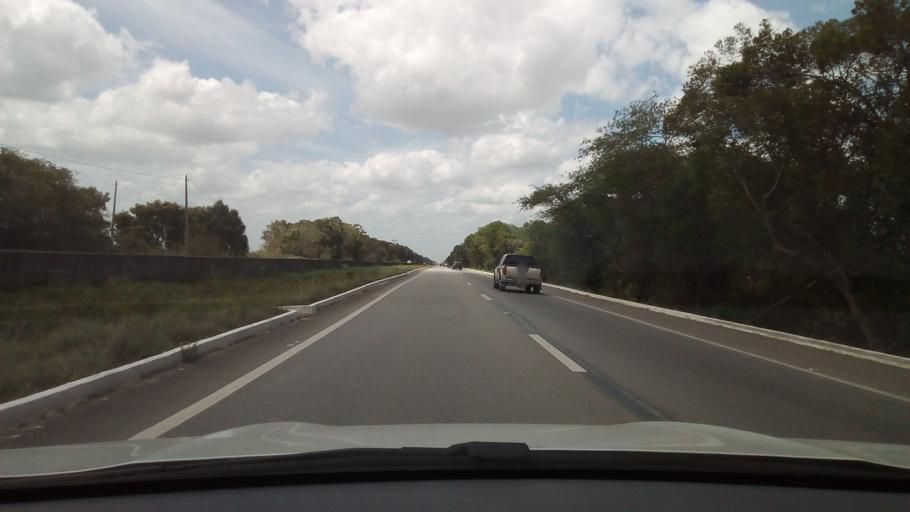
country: BR
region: Paraiba
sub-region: Mamanguape
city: Mamanguape
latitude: -6.9216
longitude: -35.1087
